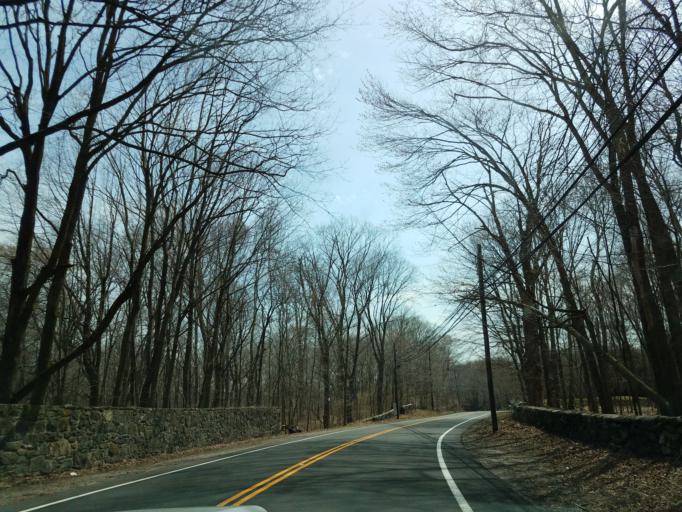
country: US
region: Connecticut
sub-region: Fairfield County
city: Glenville
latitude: 41.0373
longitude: -73.6509
